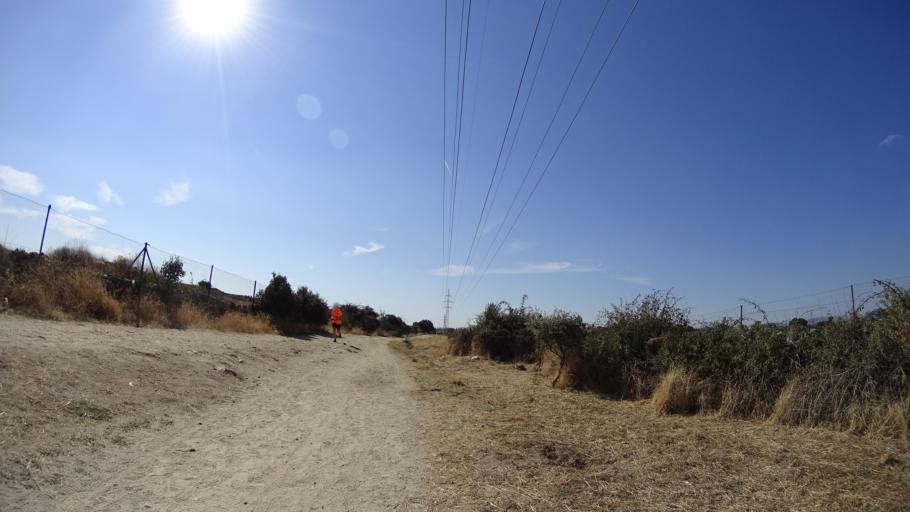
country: ES
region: Madrid
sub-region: Provincia de Madrid
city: Collado-Villalba
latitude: 40.6175
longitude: -4.0206
